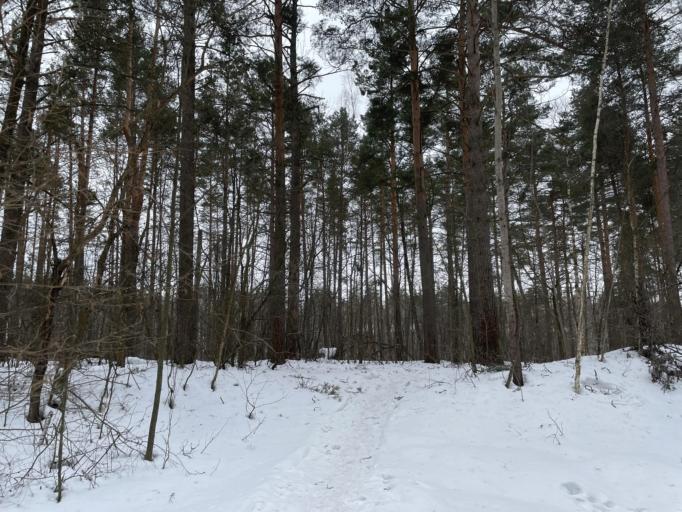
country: RU
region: Vladimir
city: Pokrov
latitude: 55.9441
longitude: 39.2410
